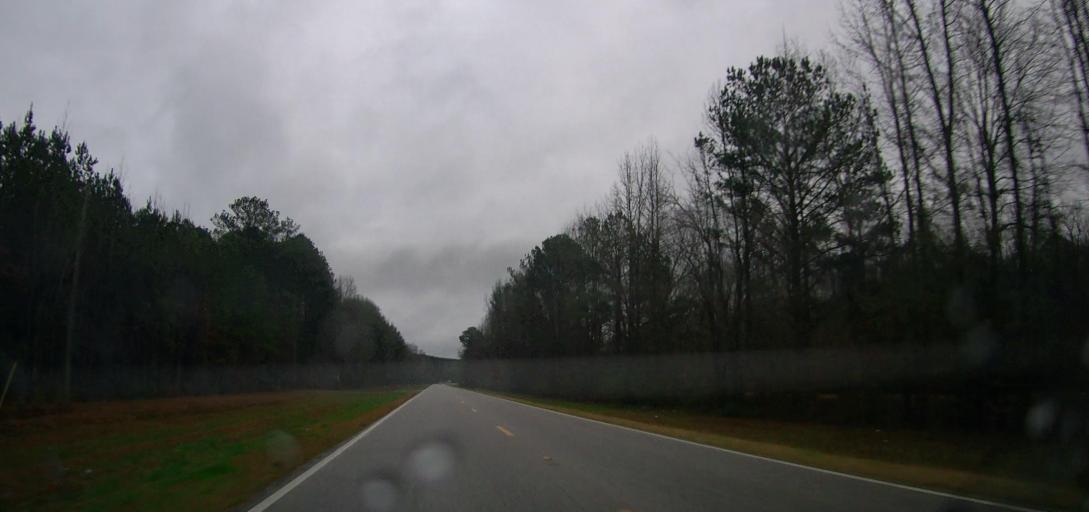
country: US
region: Alabama
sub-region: Bibb County
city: Centreville
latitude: 32.9231
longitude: -87.0386
